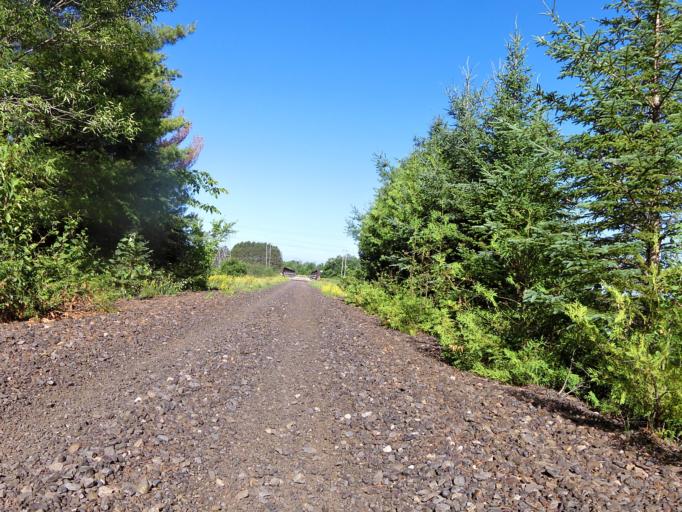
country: CA
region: Ontario
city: Arnprior
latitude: 45.4597
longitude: -76.2304
